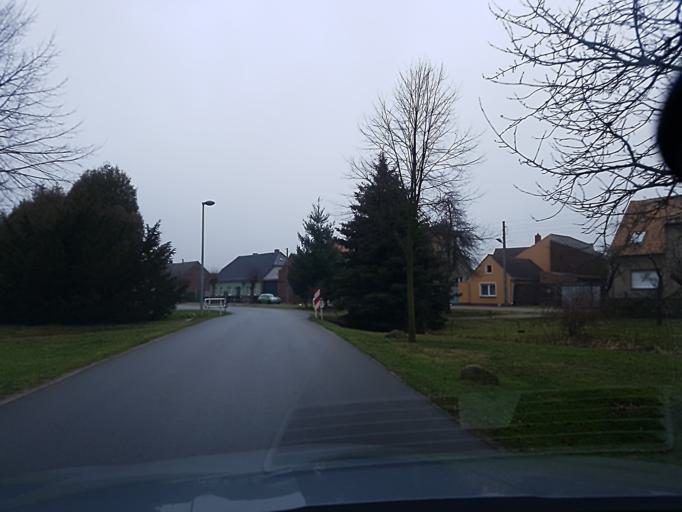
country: DE
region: Brandenburg
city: Schonewalde
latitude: 51.6586
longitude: 13.5928
